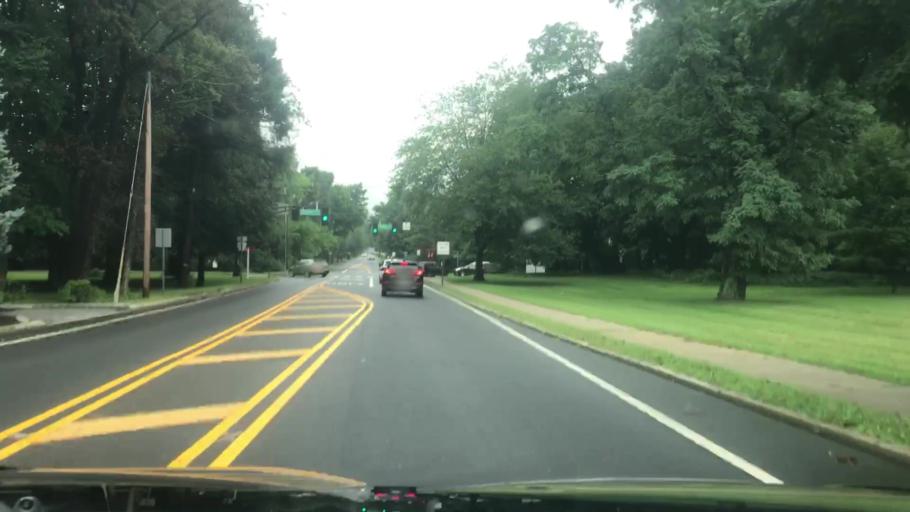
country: US
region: New Jersey
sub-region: Monmouth County
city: Little Silver
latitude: 40.3476
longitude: -74.0521
